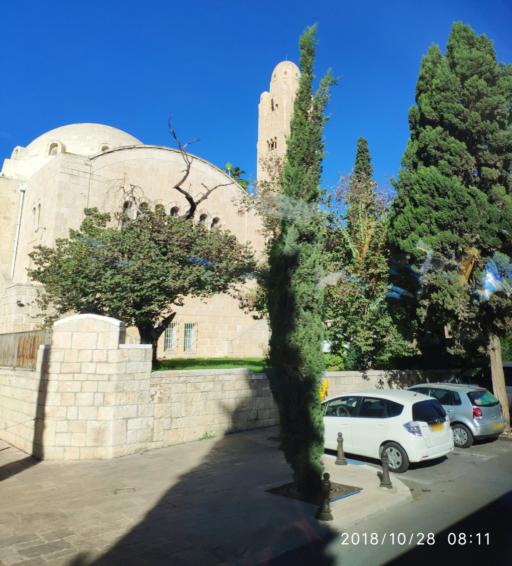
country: IL
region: Jerusalem
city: Jerusalem
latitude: 31.7738
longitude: 35.2222
